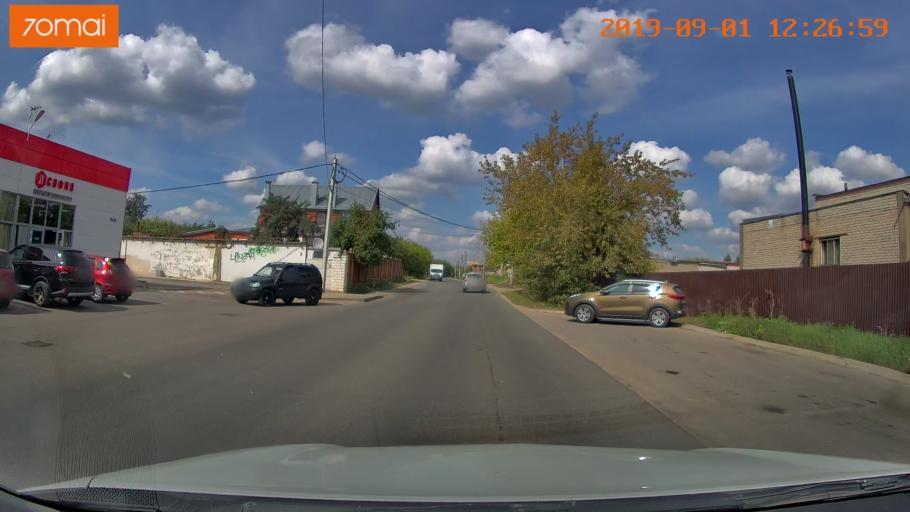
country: RU
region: Kaluga
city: Maloyaroslavets
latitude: 55.0038
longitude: 36.4616
